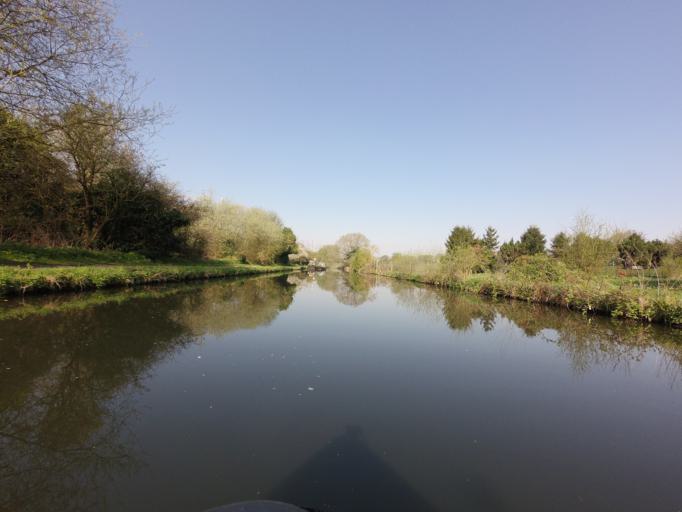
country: GB
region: England
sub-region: Hertfordshire
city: Hemel Hempstead
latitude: 51.7459
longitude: -0.5054
